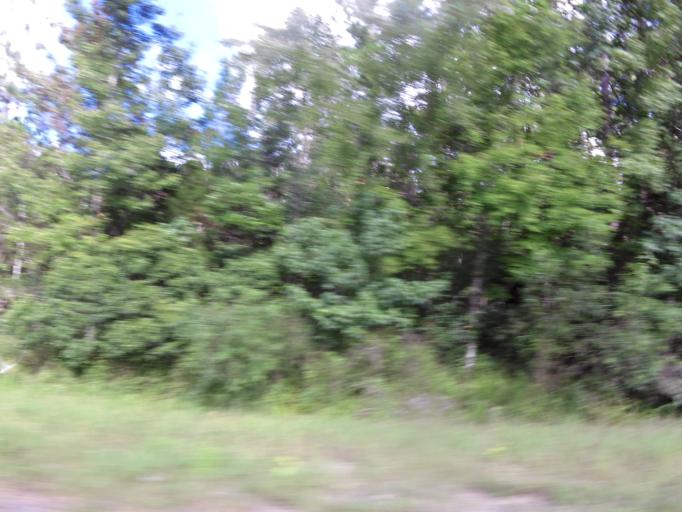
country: US
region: Georgia
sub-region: Camden County
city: Kingsland
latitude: 30.8240
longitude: -81.6950
